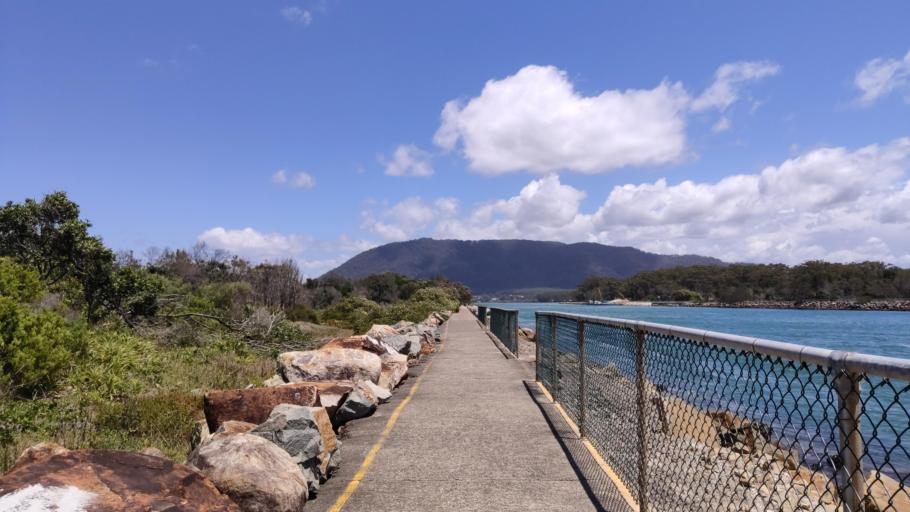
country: AU
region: New South Wales
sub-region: Port Macquarie-Hastings
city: North Haven
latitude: -31.6381
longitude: 152.8317
